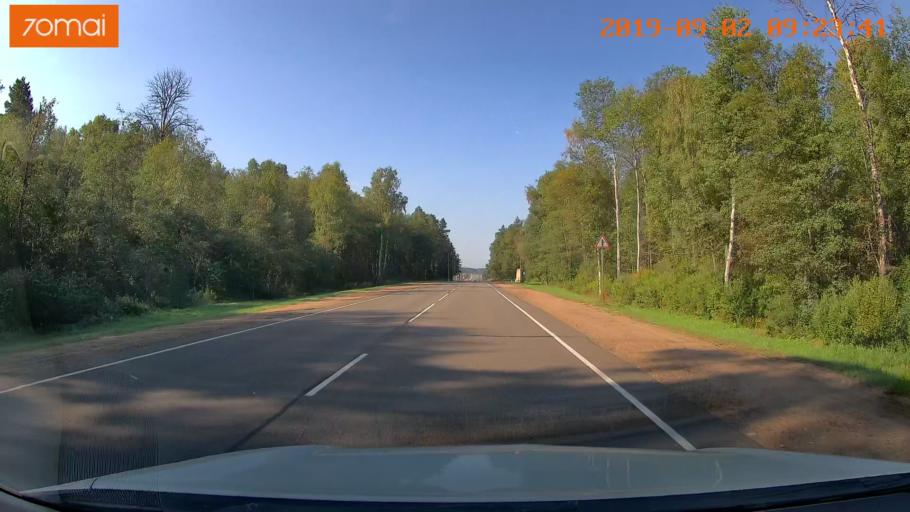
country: RU
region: Kaluga
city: Yukhnov
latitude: 54.7733
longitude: 35.3093
